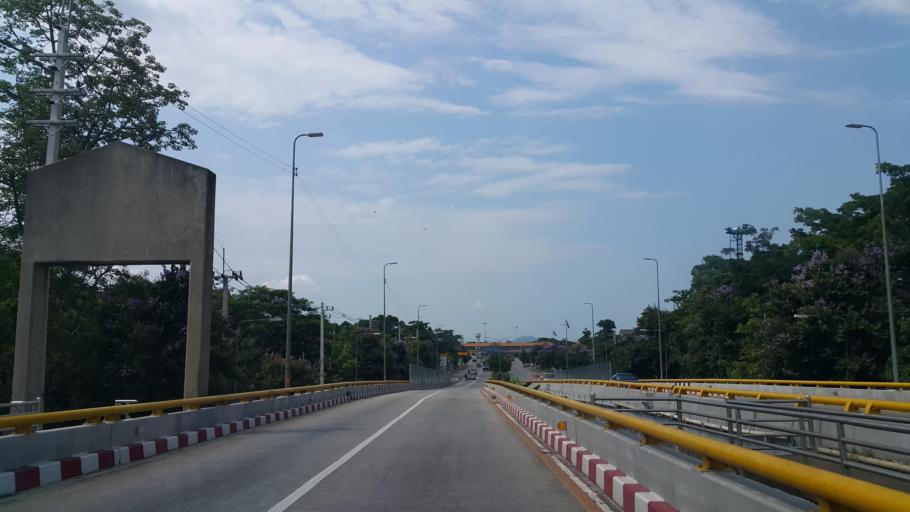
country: TH
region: Chiang Rai
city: Chiang Rai
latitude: 19.9239
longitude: 99.8619
